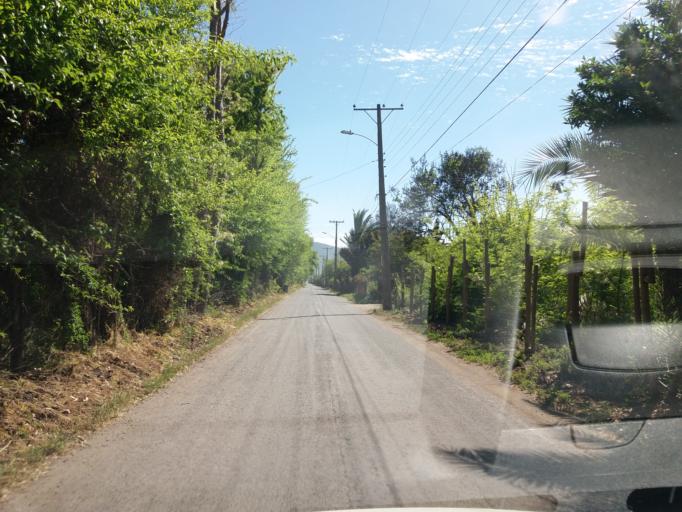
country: CL
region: Valparaiso
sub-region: Provincia de Quillota
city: Quillota
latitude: -32.8711
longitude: -71.2152
